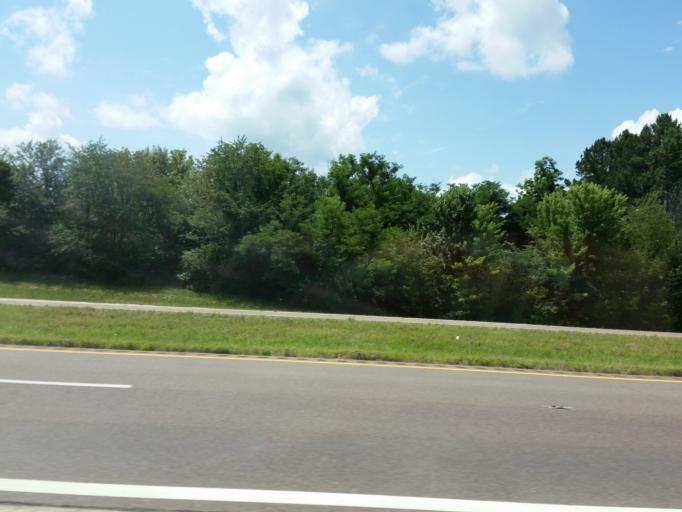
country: US
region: Tennessee
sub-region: Weakley County
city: Martin
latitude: 36.3700
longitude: -88.8552
